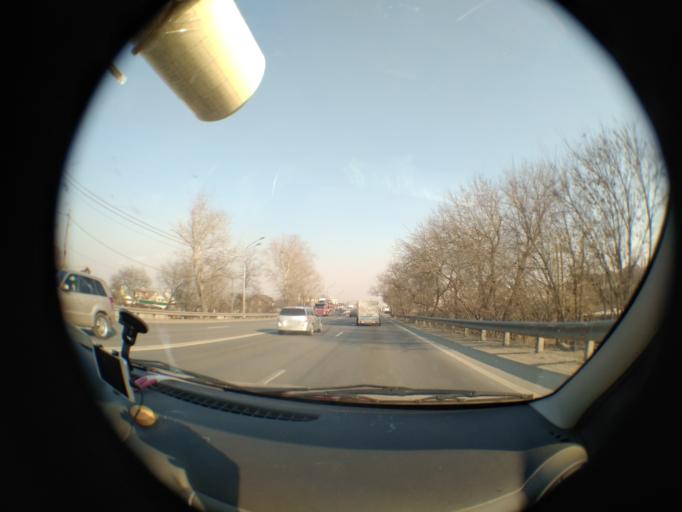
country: RU
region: Moskovskaya
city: Ostrovtsy
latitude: 55.5915
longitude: 38.0004
